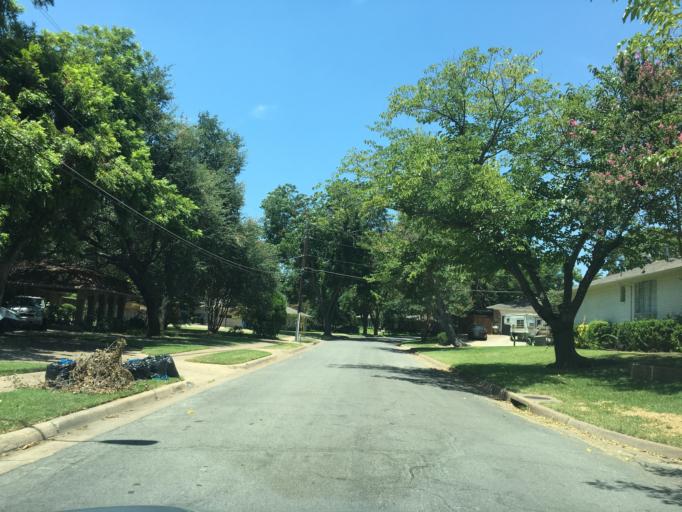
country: US
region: Texas
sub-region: Dallas County
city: Highland Park
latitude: 32.8370
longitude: -96.7403
